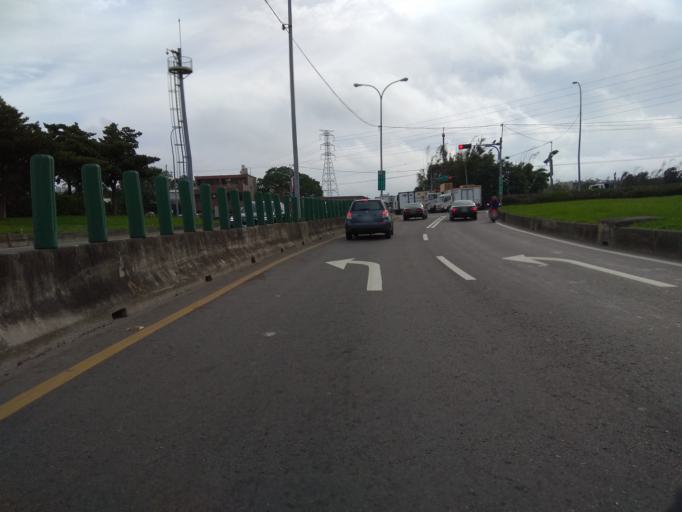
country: TW
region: Taiwan
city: Daxi
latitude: 24.8981
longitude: 121.2620
